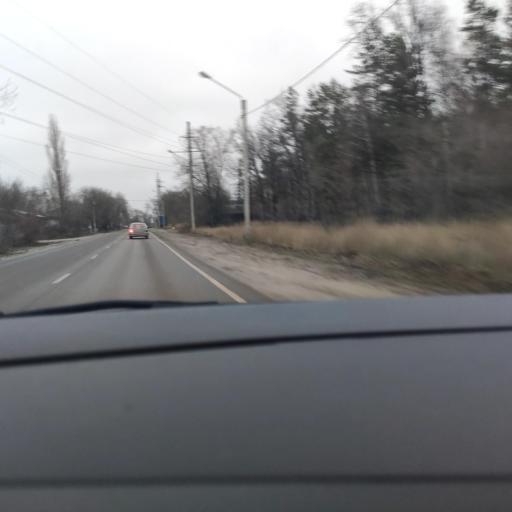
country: RU
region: Voronezj
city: Somovo
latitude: 51.7257
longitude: 39.2963
